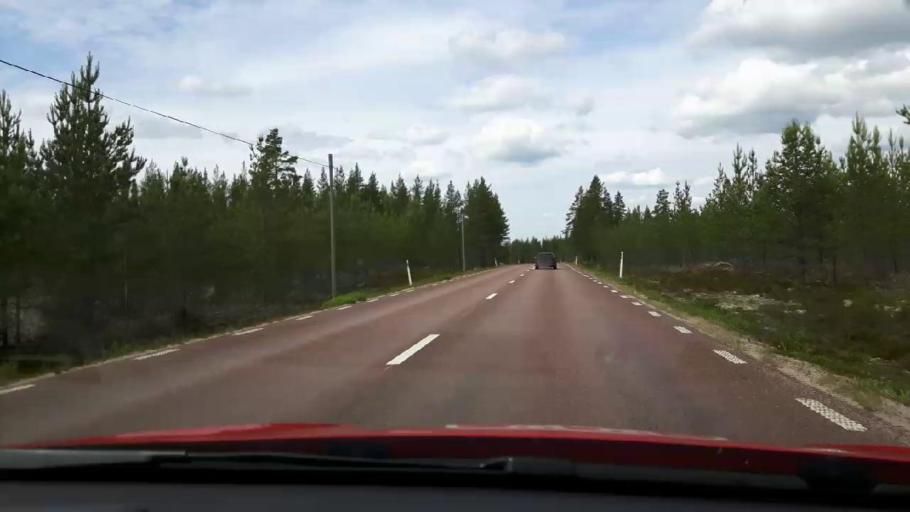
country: SE
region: Jaemtland
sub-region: Harjedalens Kommun
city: Sveg
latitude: 62.0568
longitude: 14.5934
